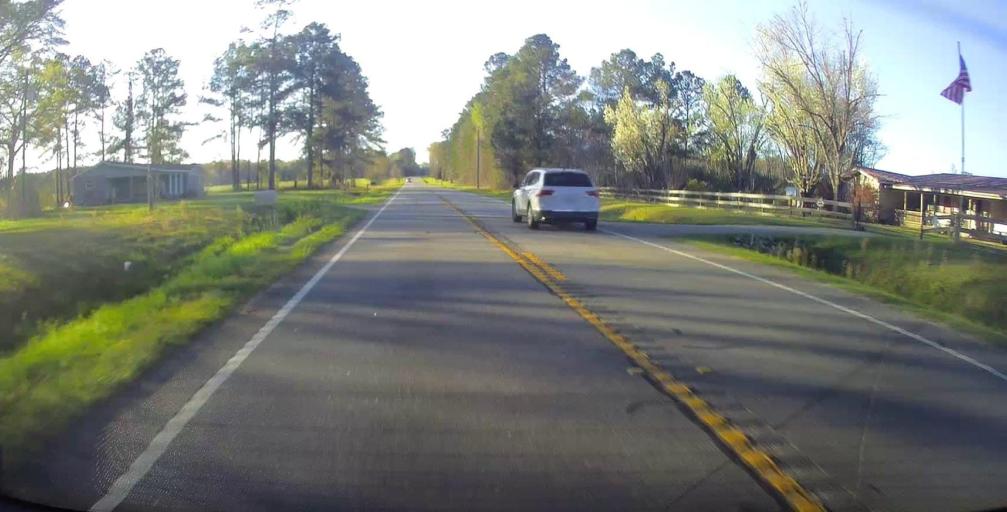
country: US
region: Georgia
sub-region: Wilcox County
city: Abbeville
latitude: 32.0532
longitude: -83.2659
